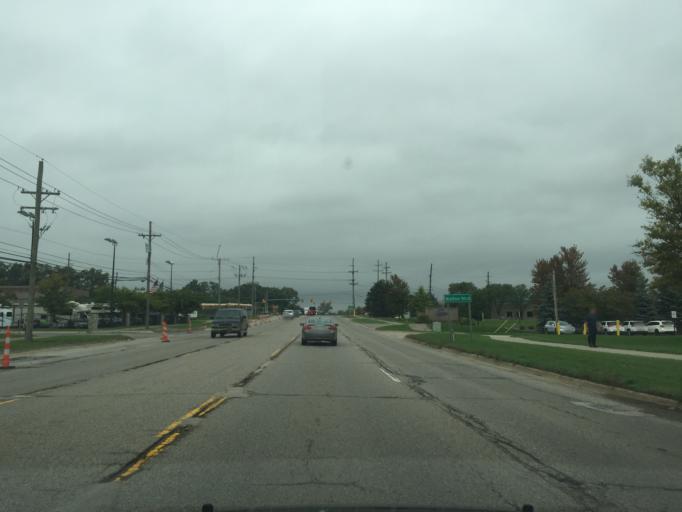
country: US
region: Michigan
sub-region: Oakland County
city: Auburn Hills
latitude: 42.6760
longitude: -83.2459
